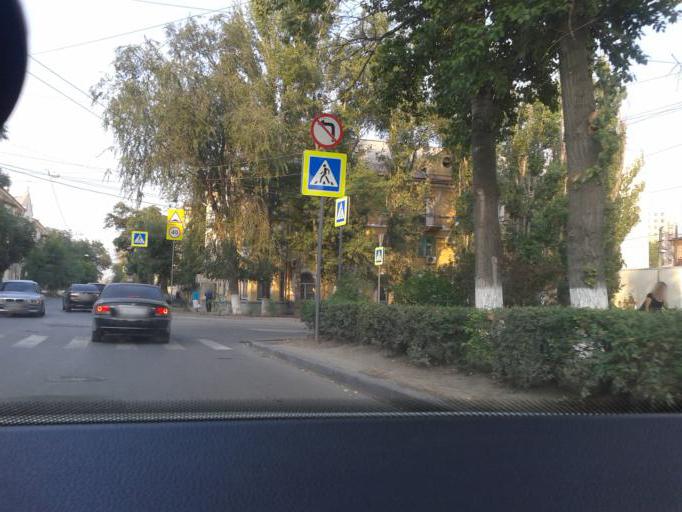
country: RU
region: Volgograd
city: Volgograd
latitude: 48.6964
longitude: 44.5036
